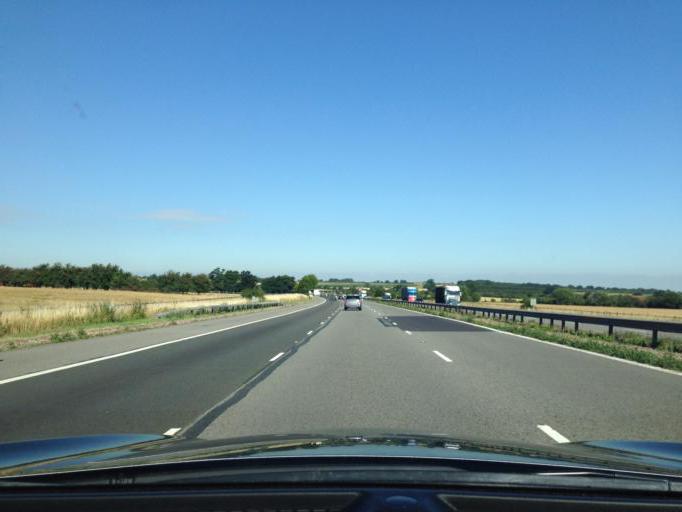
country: GB
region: England
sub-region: Oxfordshire
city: Thame
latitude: 51.7153
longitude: -1.0227
